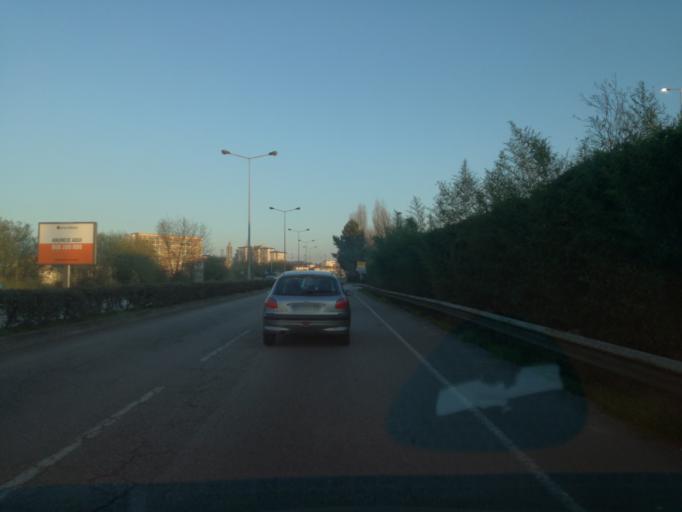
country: PT
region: Porto
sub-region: Valongo
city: Ermesinde
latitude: 41.2211
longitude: -8.5626
